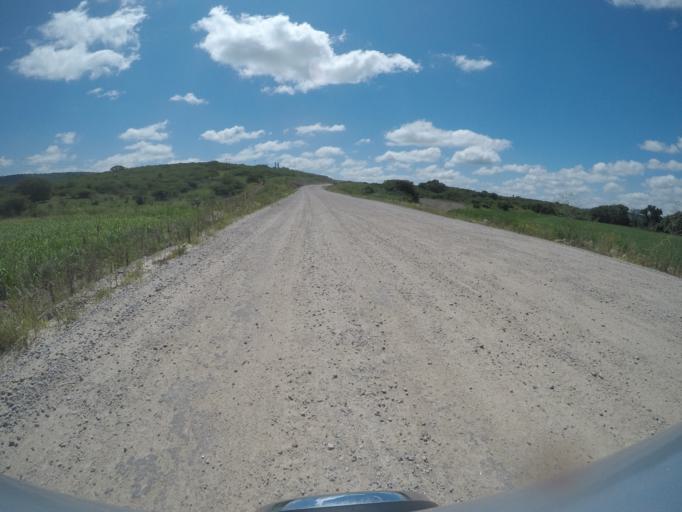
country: ZA
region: KwaZulu-Natal
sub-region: uThungulu District Municipality
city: Empangeni
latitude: -28.6426
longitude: 31.7654
